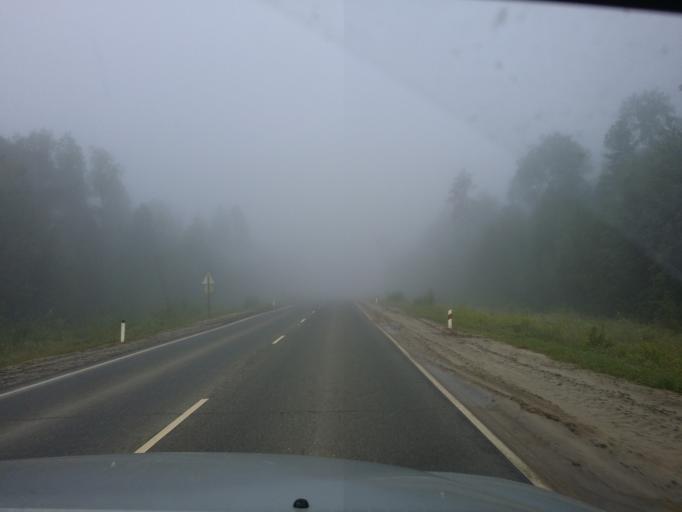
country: RU
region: Khanty-Mansiyskiy Avtonomnyy Okrug
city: Gornopravdinsk
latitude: 59.6503
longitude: 69.9173
